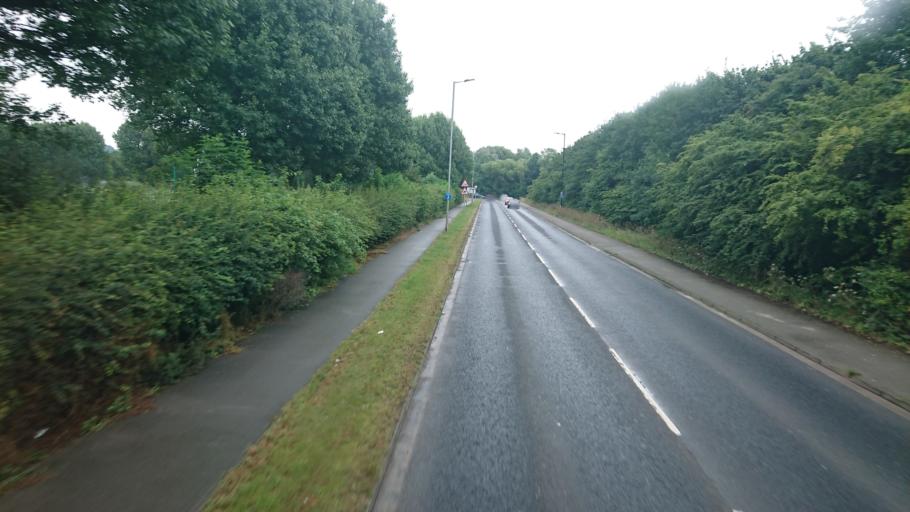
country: GB
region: England
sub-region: Rotherham
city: Orgreave
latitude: 53.3885
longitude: -1.3675
